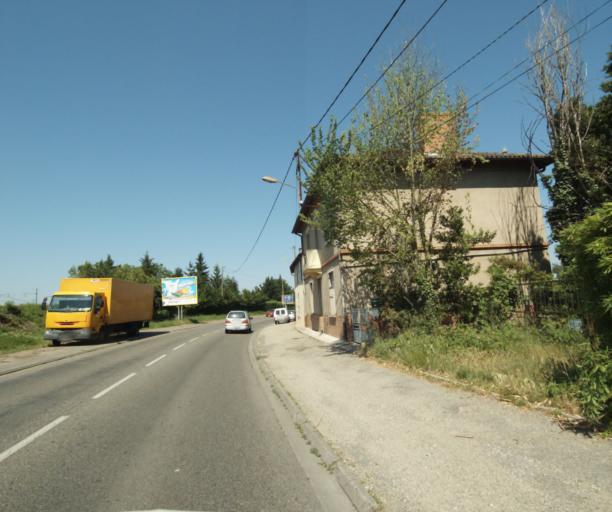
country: FR
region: Midi-Pyrenees
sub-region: Departement du Tarn-et-Garonne
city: Montauban
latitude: 44.0180
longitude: 1.3337
